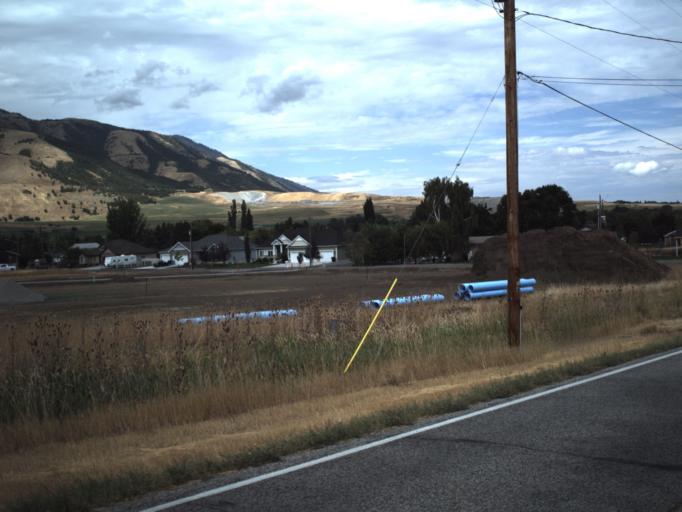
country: US
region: Utah
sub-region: Cache County
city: Wellsville
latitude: 41.6209
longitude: -111.9350
